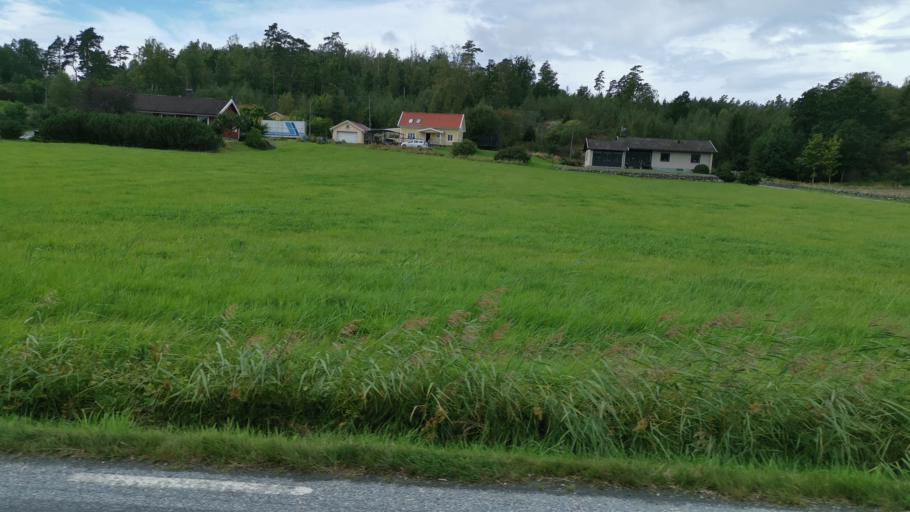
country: SE
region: Vaestra Goetaland
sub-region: Tjorns Kommun
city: Myggenas
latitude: 58.0366
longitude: 11.6538
